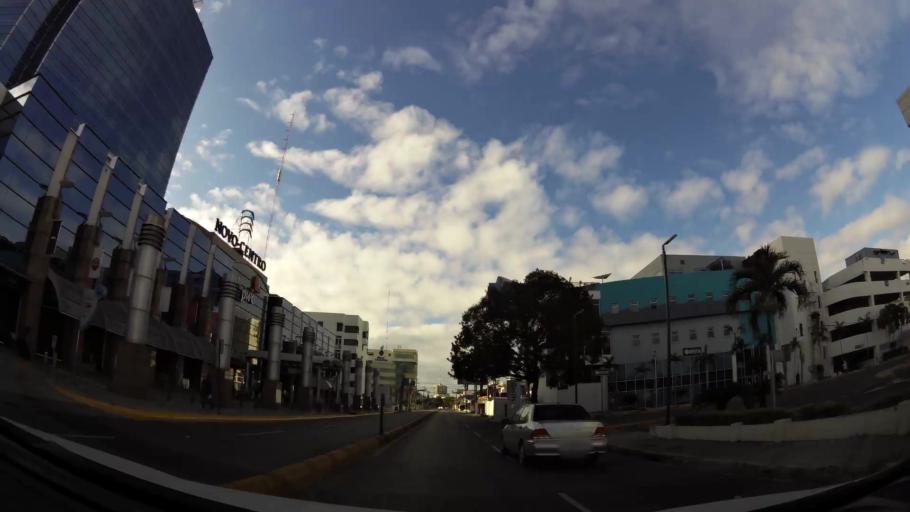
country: DO
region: Nacional
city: La Julia
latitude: 18.4736
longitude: -69.9315
